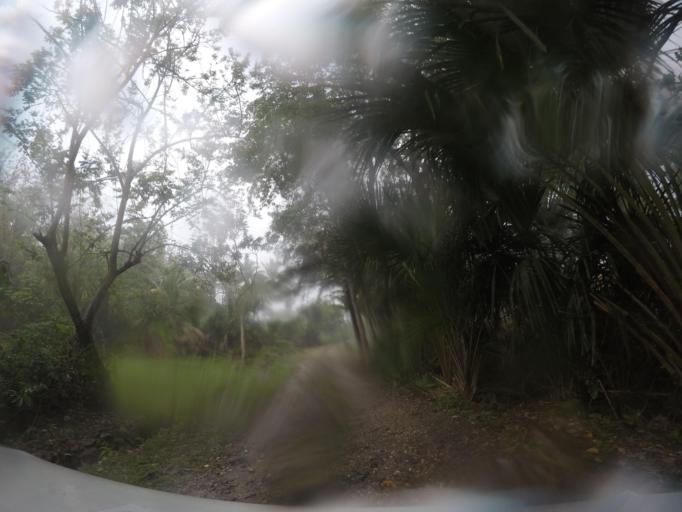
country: TL
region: Baucau
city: Venilale
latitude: -8.6372
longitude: 126.4385
